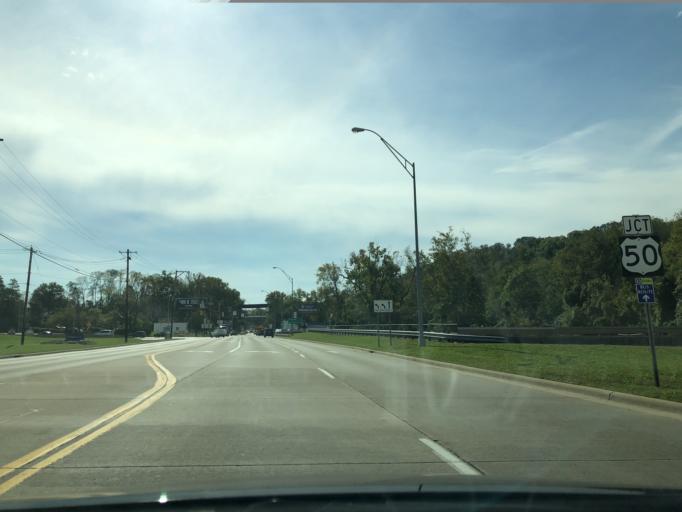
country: US
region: Ohio
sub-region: Hamilton County
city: Fairfax
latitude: 39.1413
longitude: -84.4047
